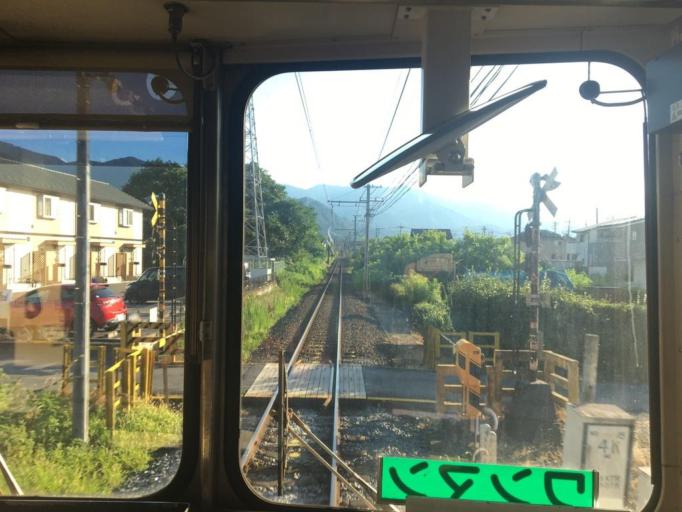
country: JP
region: Saitama
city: Chichibu
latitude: 35.9766
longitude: 139.0740
